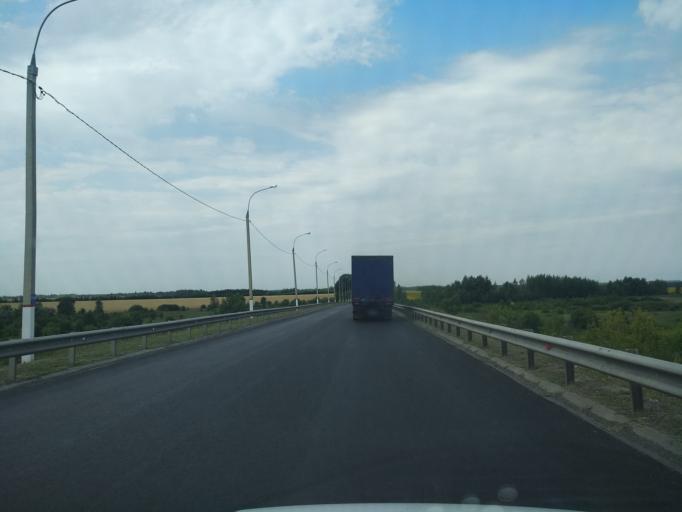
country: RU
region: Voronezj
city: Pereleshino
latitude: 51.7607
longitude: 40.1245
